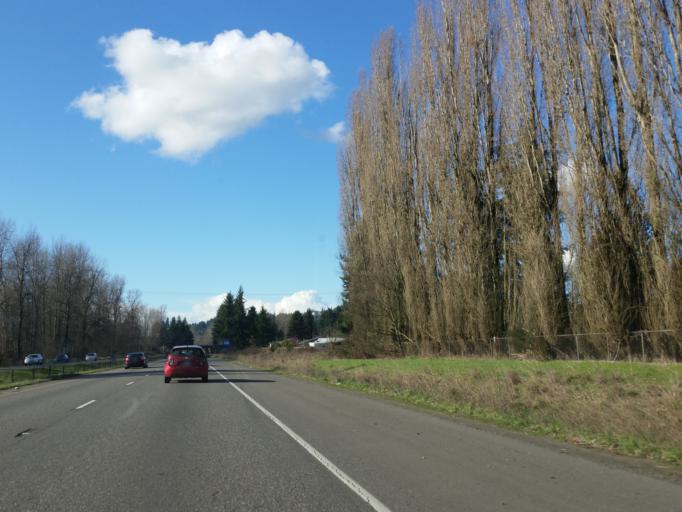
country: US
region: Washington
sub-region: Pierce County
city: Sumner
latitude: 47.1945
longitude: -122.2417
